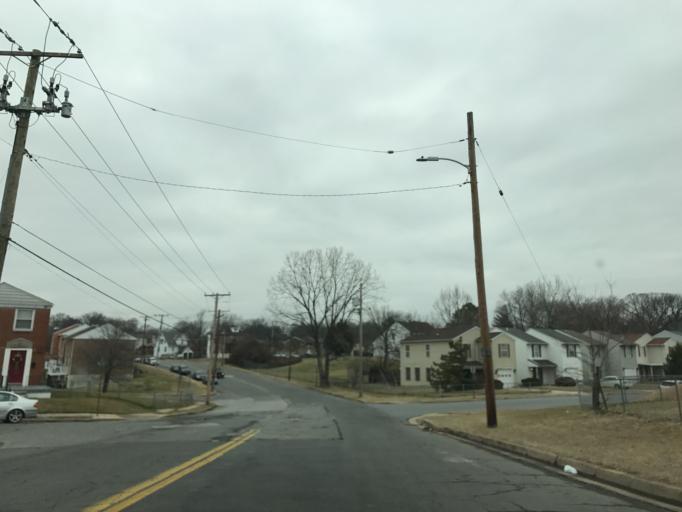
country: US
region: Maryland
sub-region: Baltimore County
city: Rosedale
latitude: 39.3354
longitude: -76.5298
